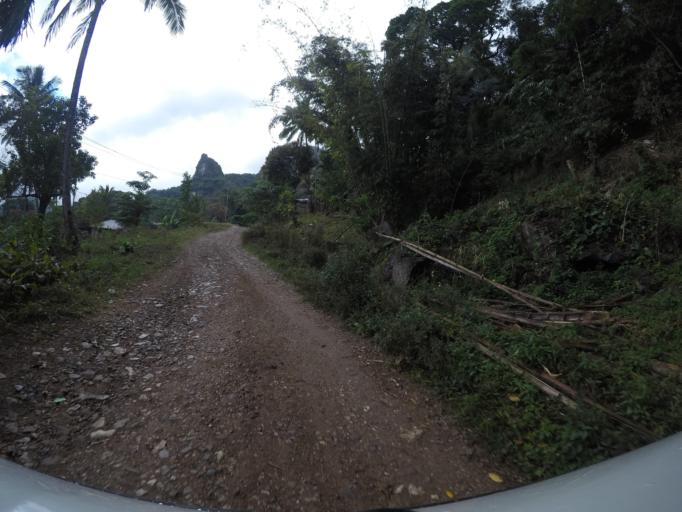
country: TL
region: Baucau
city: Baucau
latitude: -8.6457
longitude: 126.6291
